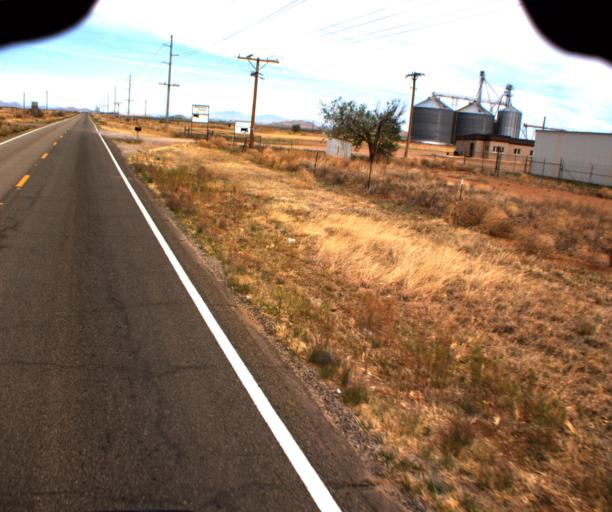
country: US
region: Arizona
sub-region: Cochise County
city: Tombstone
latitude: 31.7632
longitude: -109.6899
